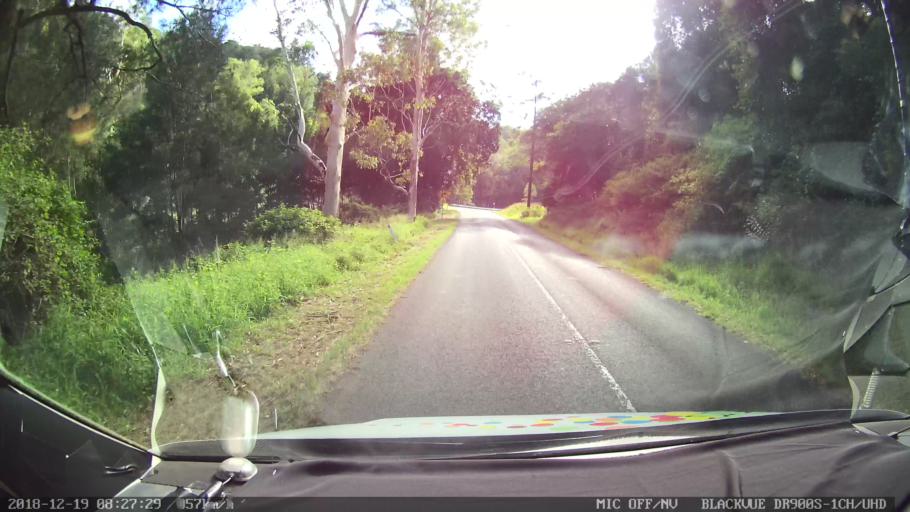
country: AU
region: New South Wales
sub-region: Kyogle
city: Kyogle
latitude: -28.3189
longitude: 152.9269
